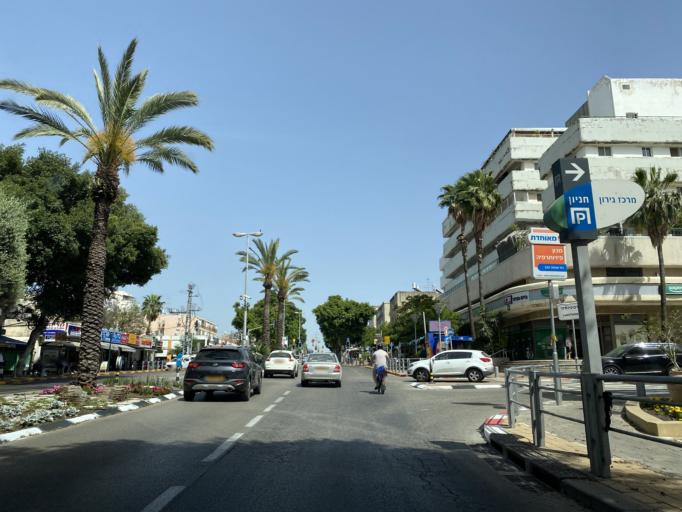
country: IL
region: Central District
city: Ra'anana
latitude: 32.1806
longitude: 34.8739
